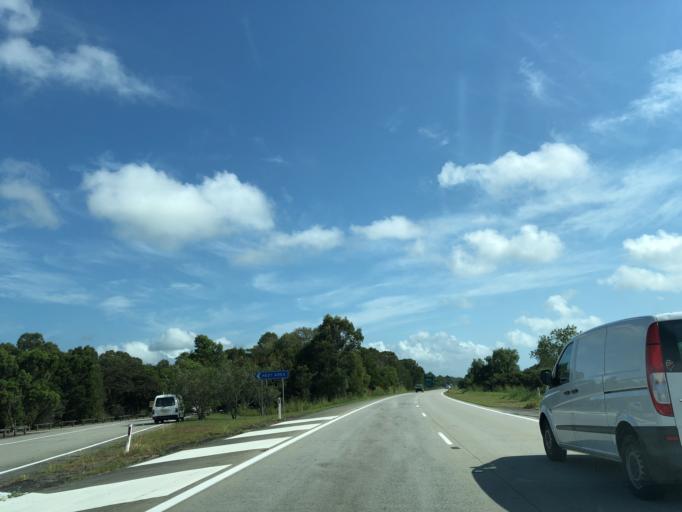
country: AU
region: New South Wales
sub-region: Byron Shire
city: Brunswick Heads
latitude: -28.5993
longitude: 153.5448
